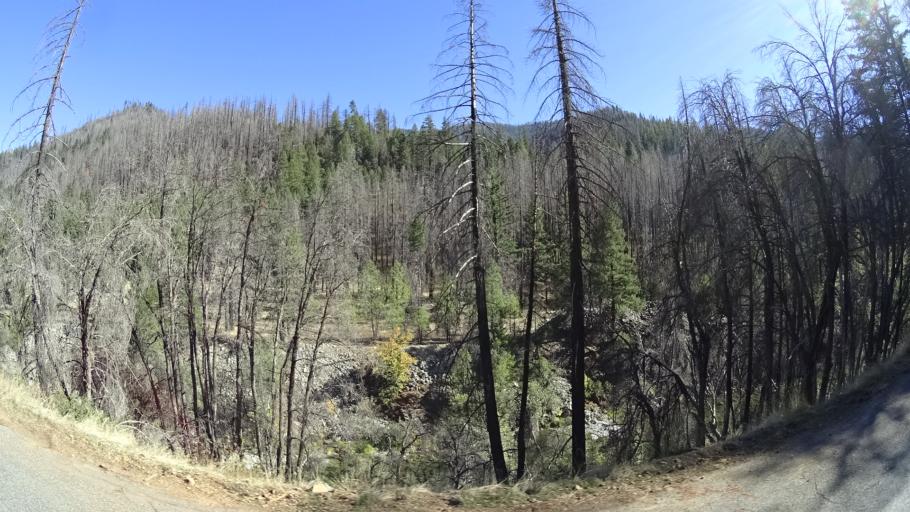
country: US
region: California
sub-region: Siskiyou County
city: Happy Camp
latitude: 41.3117
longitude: -123.0676
